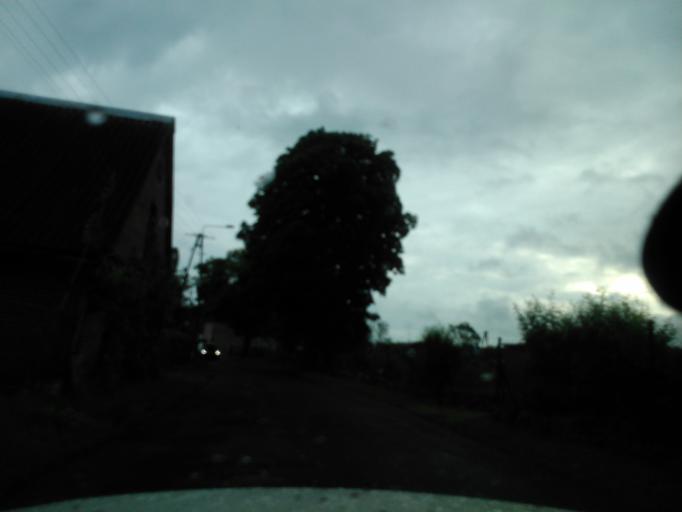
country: PL
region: Pomeranian Voivodeship
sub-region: Powiat slupski
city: Smoldzino
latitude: 54.6490
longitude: 17.2522
